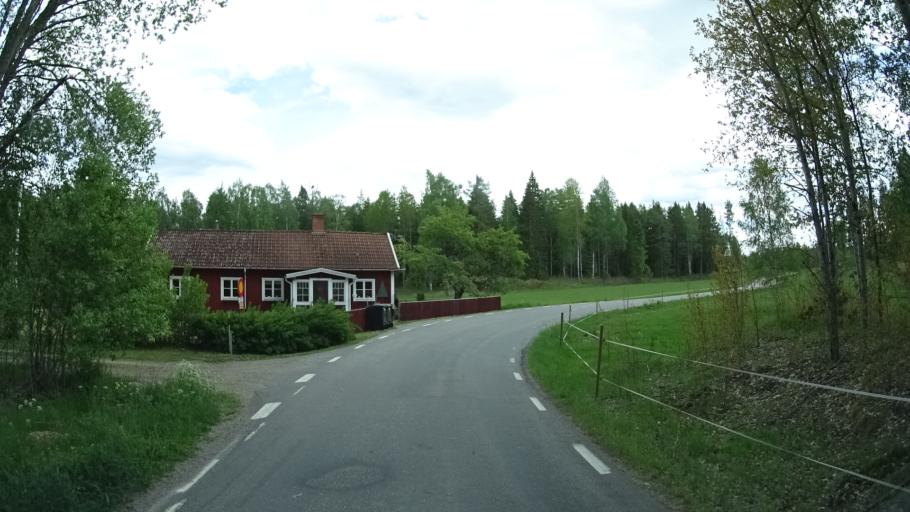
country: SE
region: OEstergoetland
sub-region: Finspangs Kommun
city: Finspang
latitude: 58.6034
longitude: 15.7561
